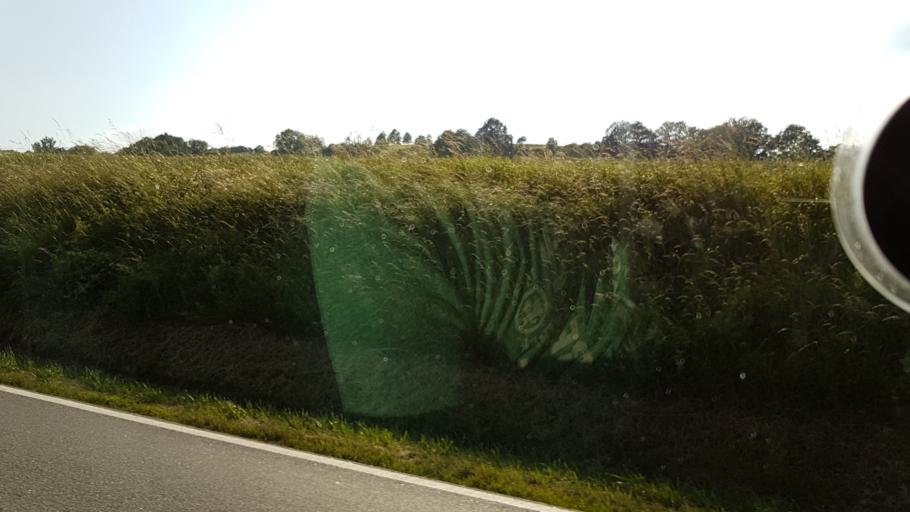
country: DE
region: Rheinland-Pfalz
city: Meisenheim
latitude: 49.6978
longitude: 7.6564
